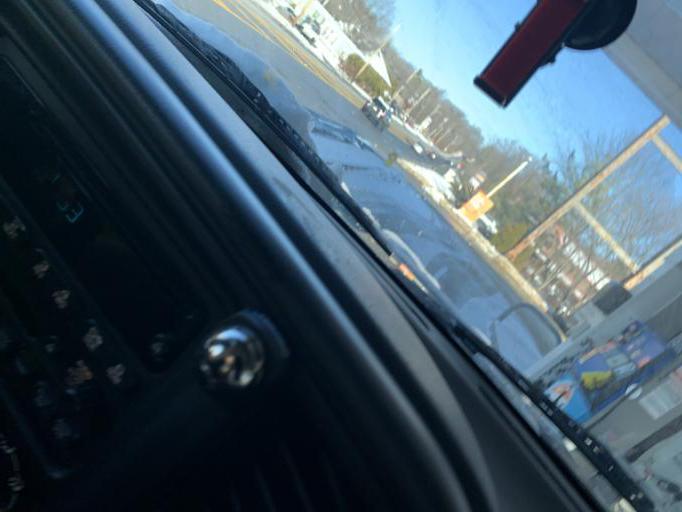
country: US
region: Massachusetts
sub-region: Essex County
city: Danvers
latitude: 42.5992
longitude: -70.9602
